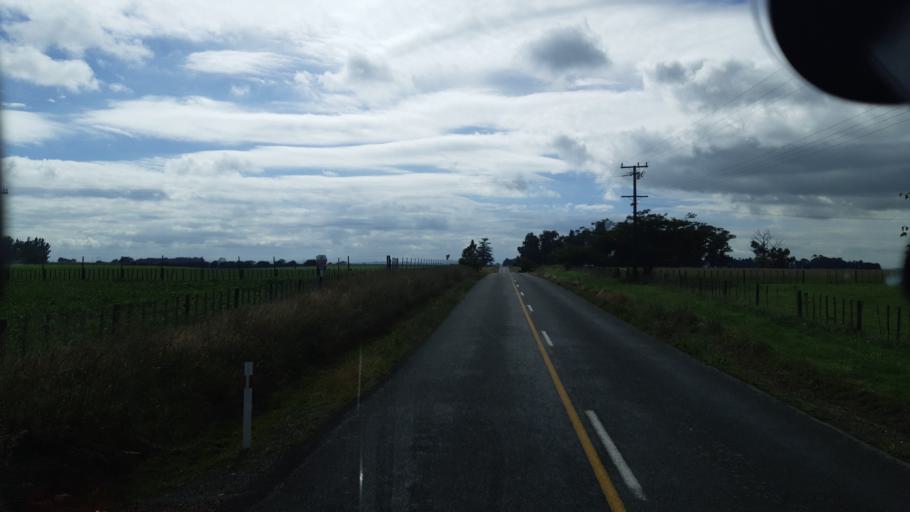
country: NZ
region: Manawatu-Wanganui
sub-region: Rangitikei District
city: Bulls
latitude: -40.0103
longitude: 175.4298
